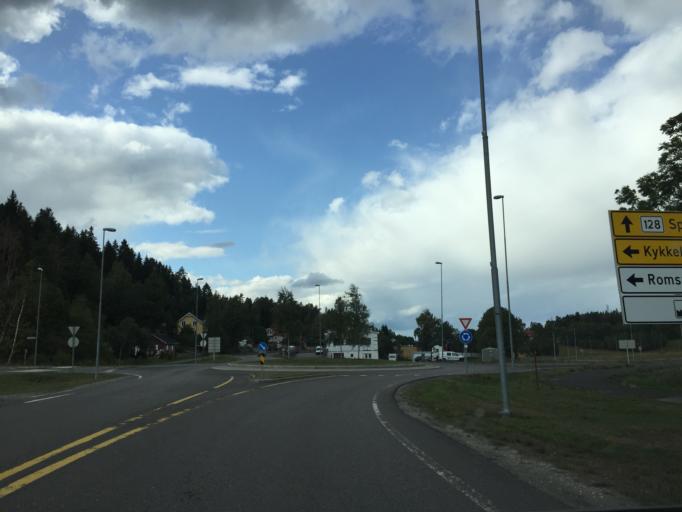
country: NO
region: Ostfold
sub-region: Spydeberg
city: Spydeberg
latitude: 59.5883
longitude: 11.1146
